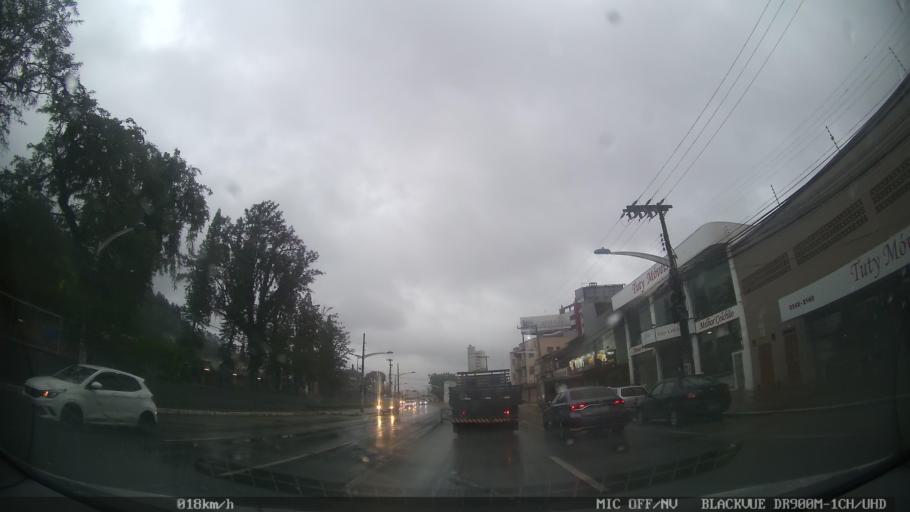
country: BR
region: Santa Catarina
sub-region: Itajai
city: Itajai
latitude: -26.9136
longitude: -48.6612
